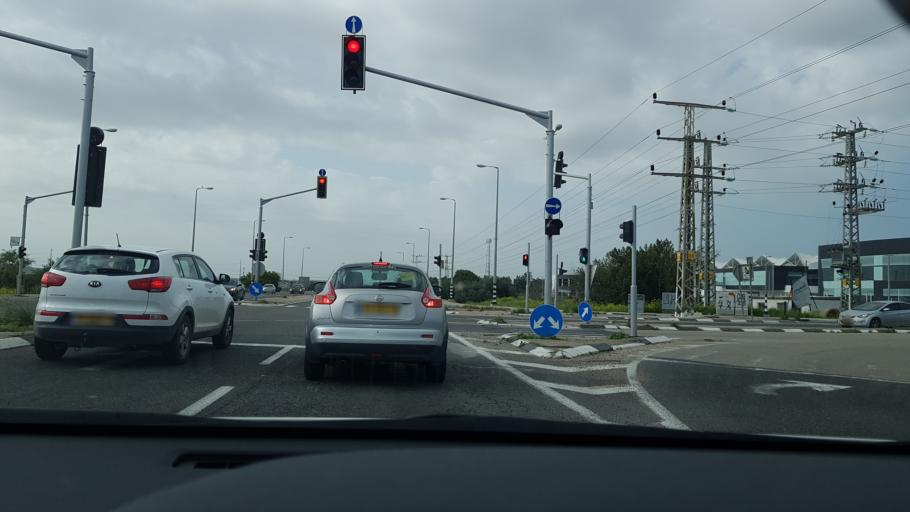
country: IL
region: Southern District
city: Ashqelon
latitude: 31.6278
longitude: 34.5856
